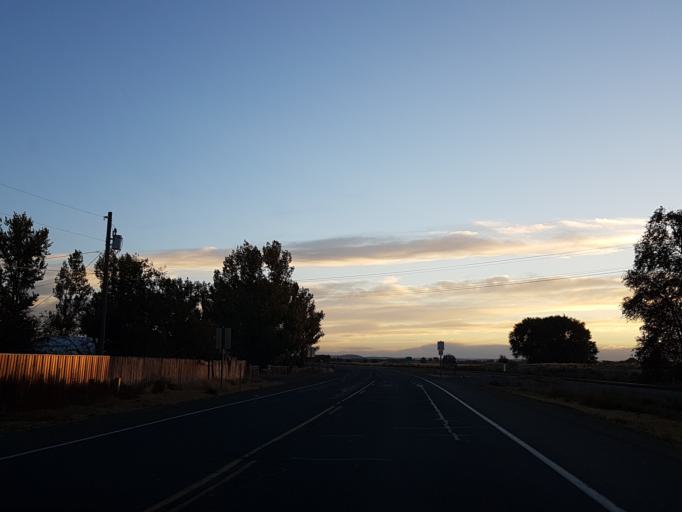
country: US
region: Oregon
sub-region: Malheur County
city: Vale
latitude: 43.9805
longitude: -117.2546
